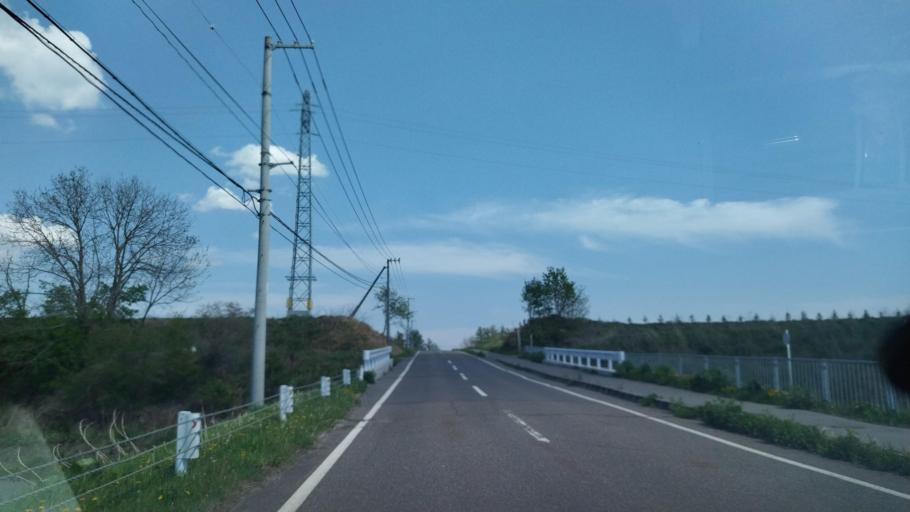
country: JP
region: Hokkaido
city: Otofuke
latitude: 43.1009
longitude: 143.2203
